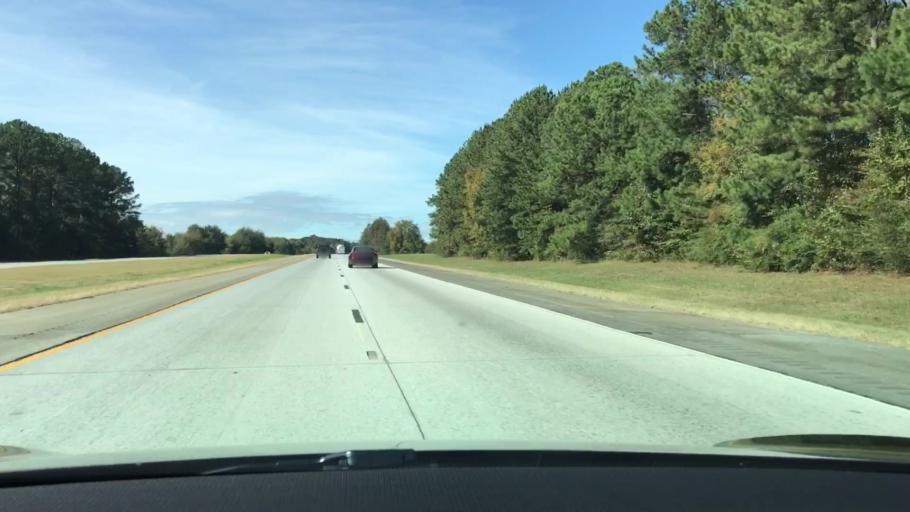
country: US
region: Georgia
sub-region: Morgan County
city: Madison
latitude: 33.5541
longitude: -83.3986
